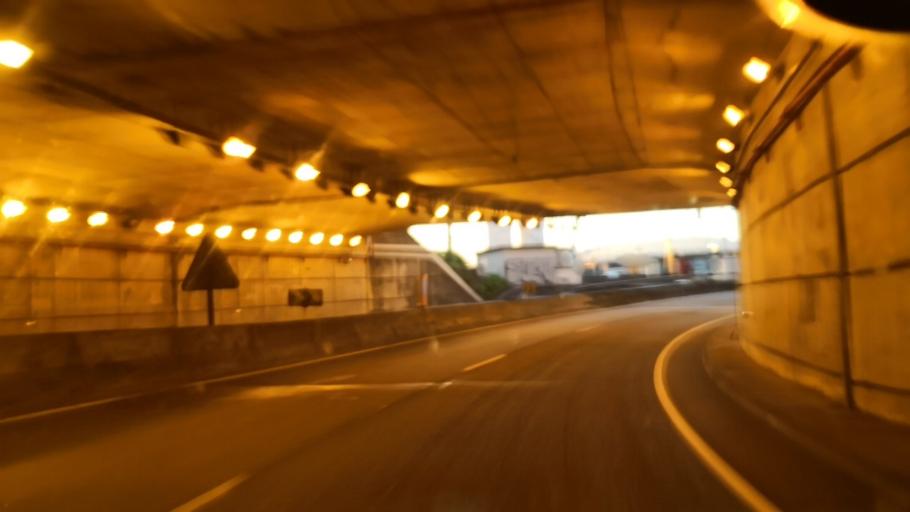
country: ES
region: Galicia
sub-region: Provincia de Pontevedra
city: Vigo
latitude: 42.2395
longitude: -8.7079
